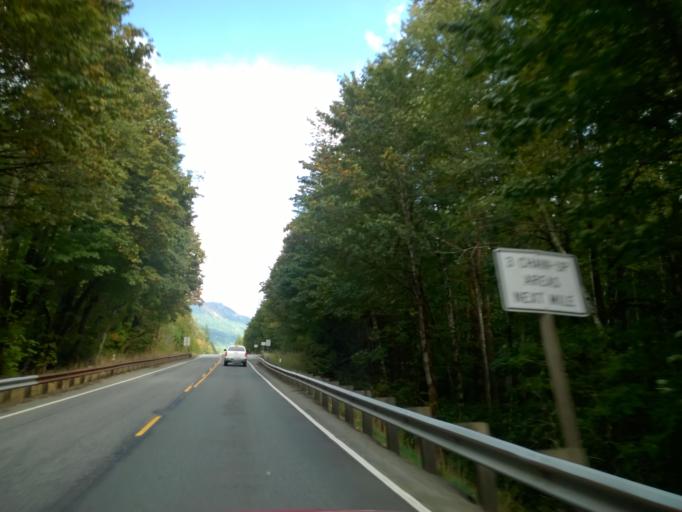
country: US
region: Washington
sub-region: Snohomish County
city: Gold Bar
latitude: 47.7153
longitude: -121.2599
